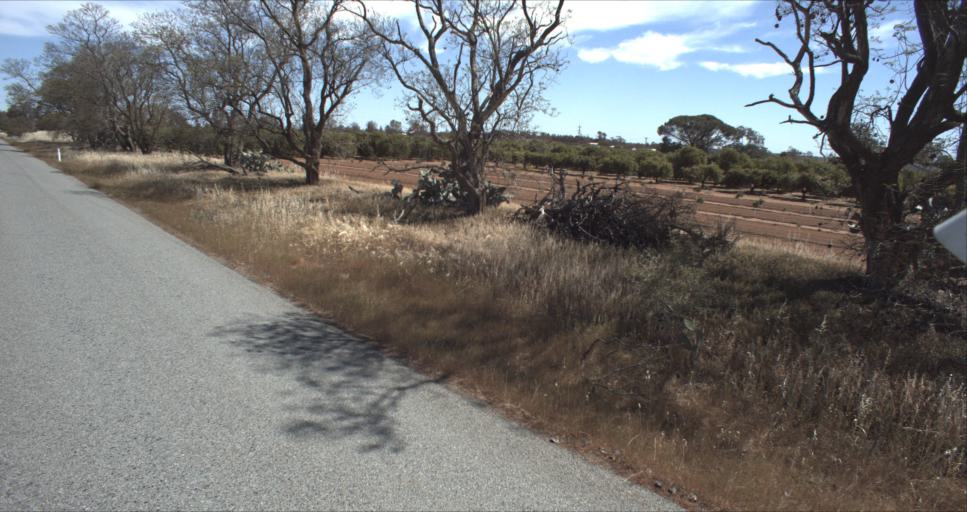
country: AU
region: New South Wales
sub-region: Leeton
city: Leeton
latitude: -34.6134
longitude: 146.4341
